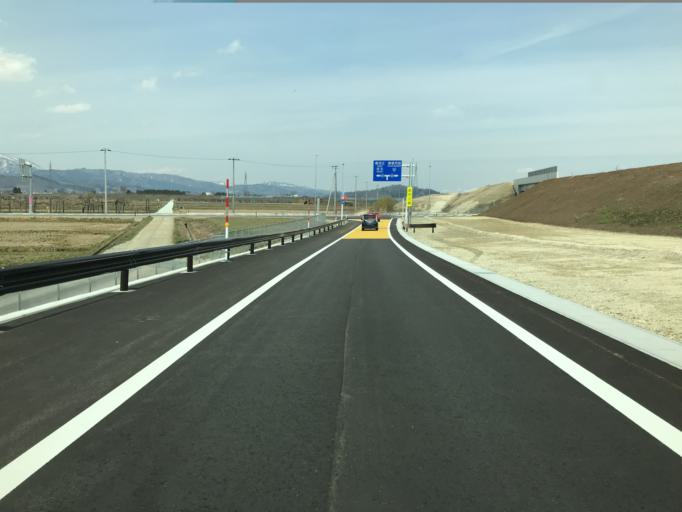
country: JP
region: Yamagata
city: Higashine
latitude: 38.4460
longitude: 140.3534
